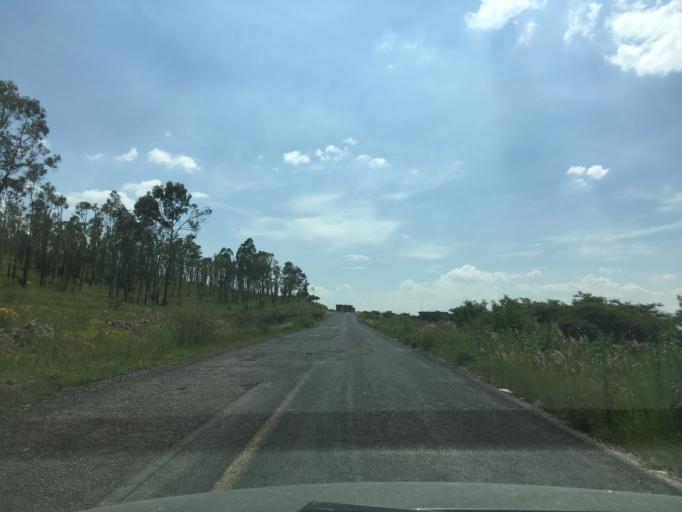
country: MX
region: Michoacan
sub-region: Morelia
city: Morelos
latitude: 19.6477
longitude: -101.2026
